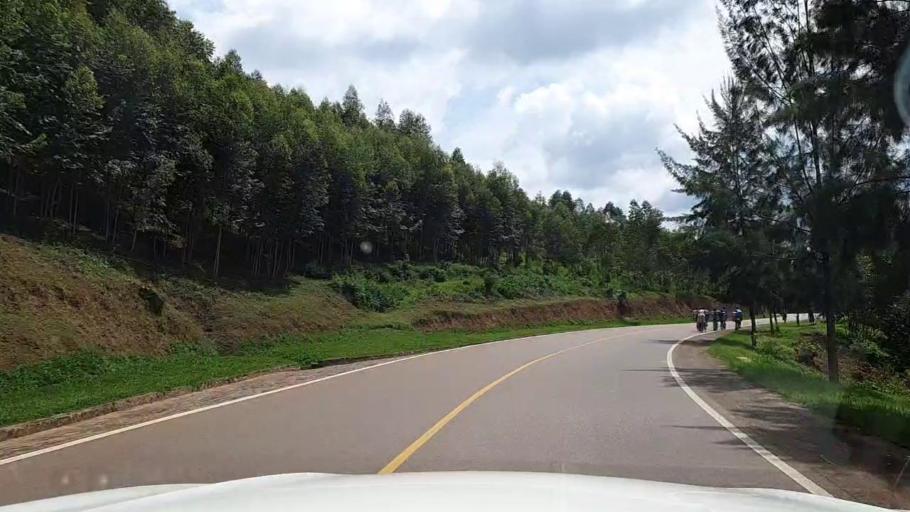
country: RW
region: Kigali
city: Kigali
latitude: -1.8127
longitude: 30.1037
